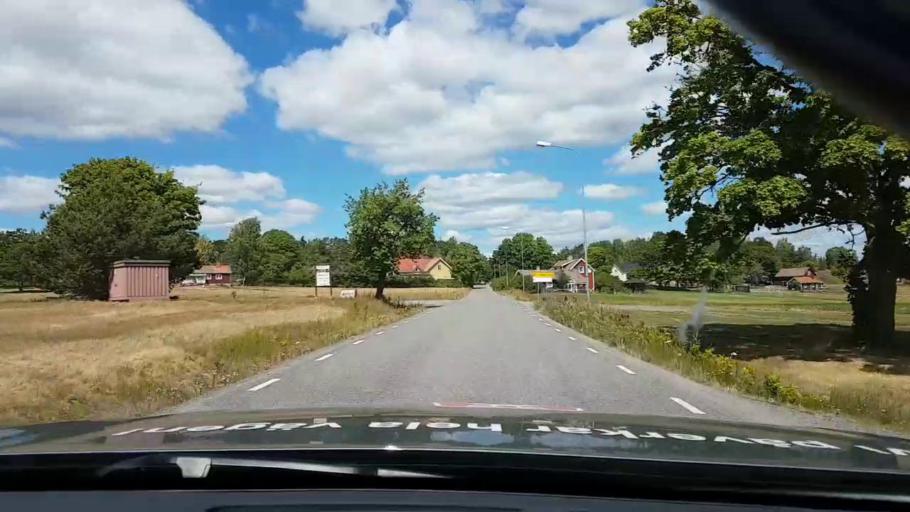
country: SE
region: Kalmar
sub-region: Vasterviks Kommun
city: Forserum
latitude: 58.0094
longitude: 16.5784
